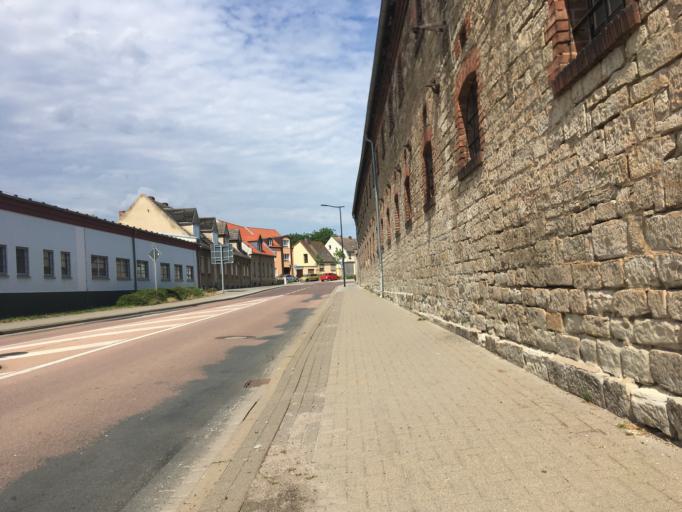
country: DE
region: Saxony-Anhalt
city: Bernburg
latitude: 51.7802
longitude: 11.7684
